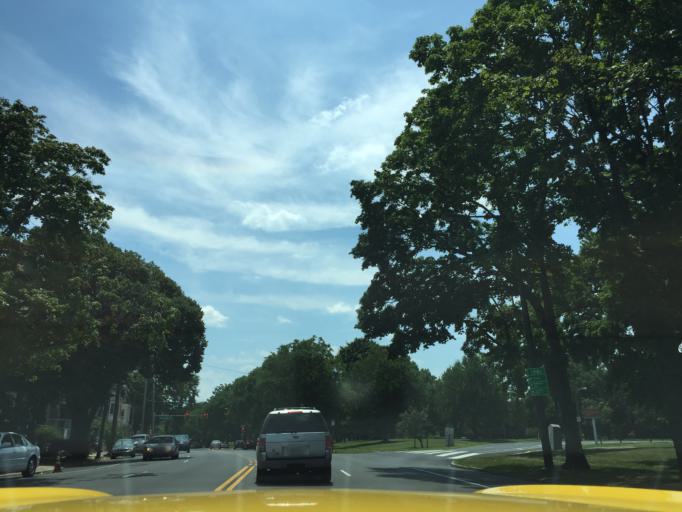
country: US
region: Pennsylvania
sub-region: Montgomery County
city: Bala-Cynwyd
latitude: 39.9962
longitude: -75.1876
